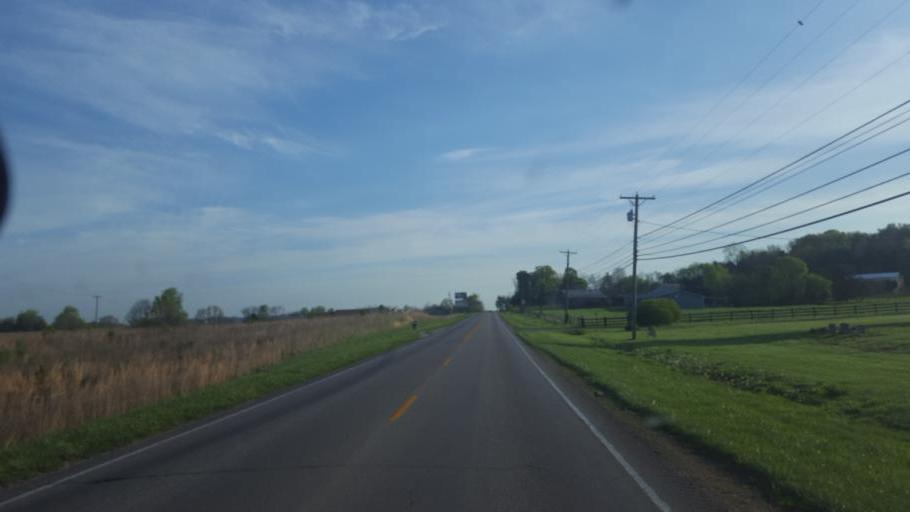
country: US
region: Kentucky
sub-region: Hart County
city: Munfordville
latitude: 37.2474
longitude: -85.8905
